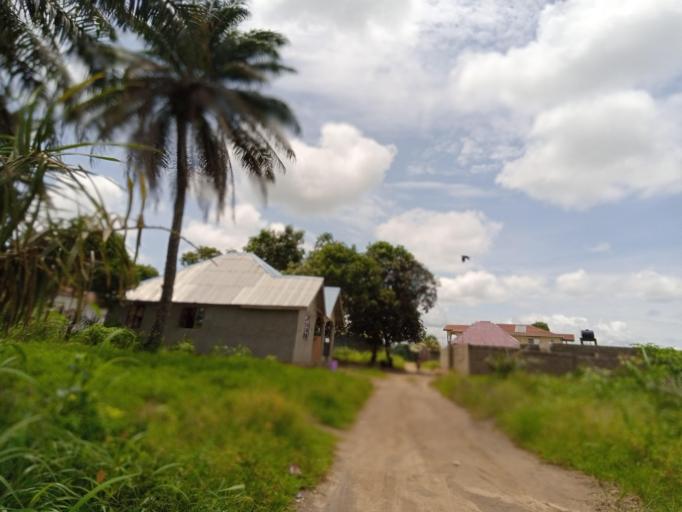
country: SL
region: Northern Province
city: Masoyila
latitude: 8.5937
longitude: -13.1831
